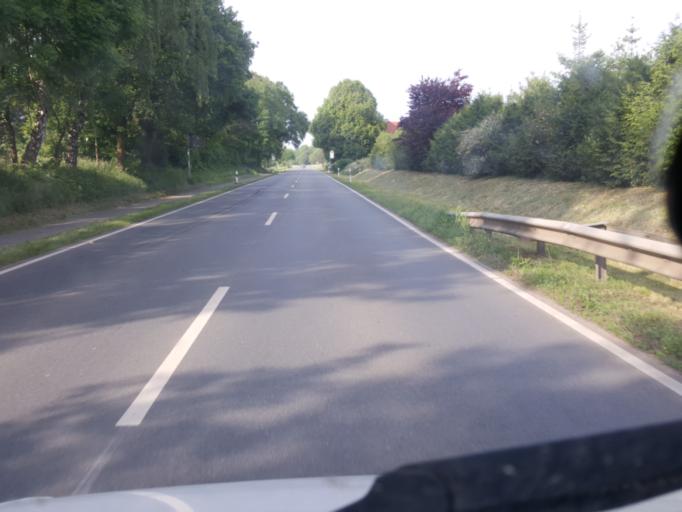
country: DE
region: Lower Saxony
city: Liebenau
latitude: 52.5923
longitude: 9.0953
